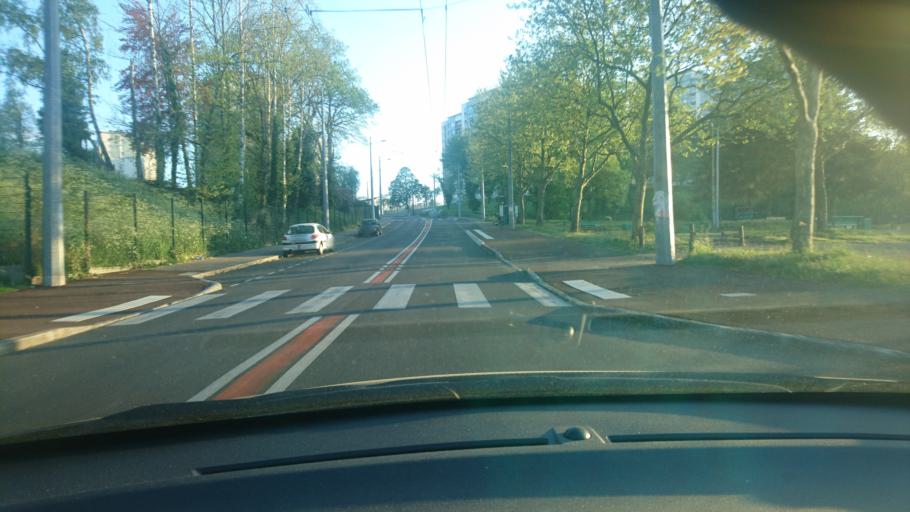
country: FR
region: Limousin
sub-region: Departement de la Haute-Vienne
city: Limoges
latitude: 45.8524
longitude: 1.2730
